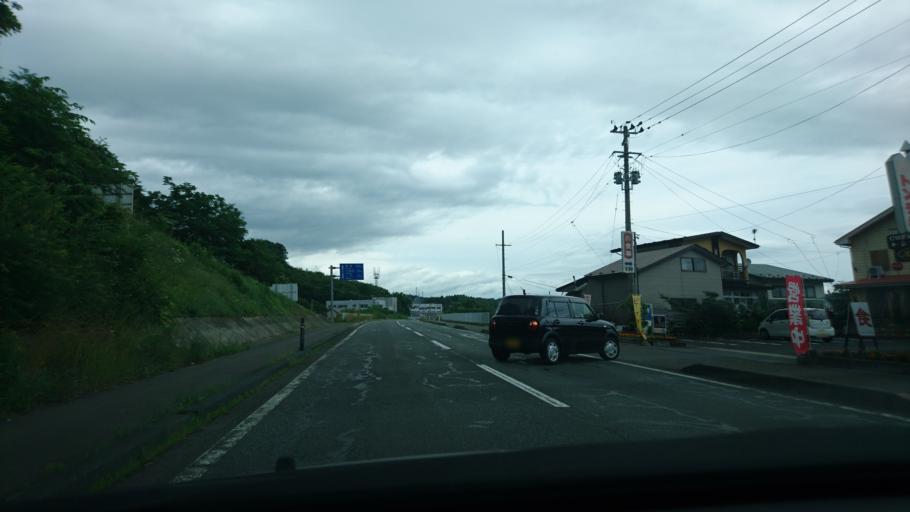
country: JP
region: Iwate
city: Morioka-shi
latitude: 39.9609
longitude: 141.2109
